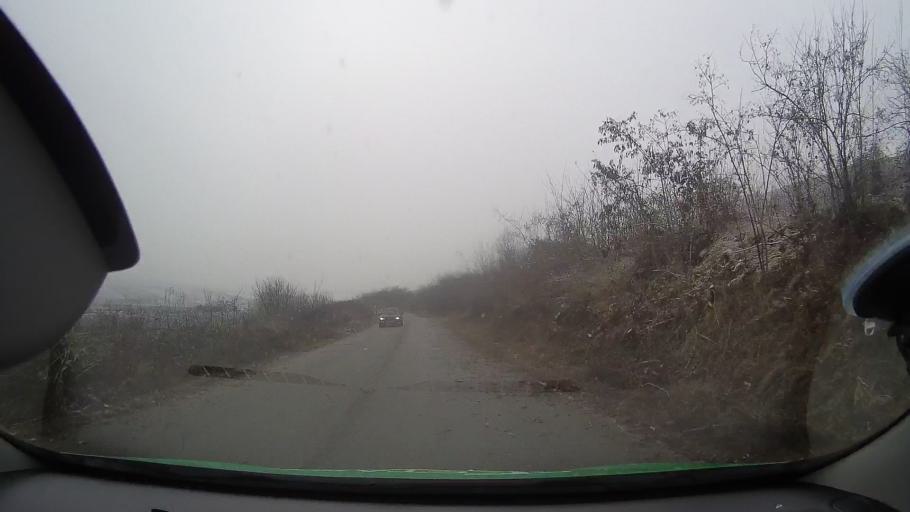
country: RO
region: Alba
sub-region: Comuna Noslac
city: Noslac
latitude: 46.3714
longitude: 23.9225
